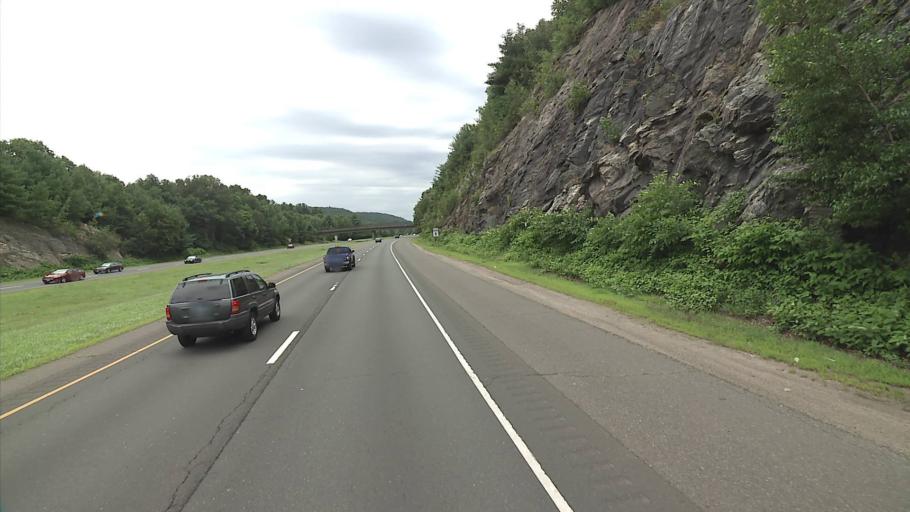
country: US
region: Connecticut
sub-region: New Haven County
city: Seymour
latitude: 41.4418
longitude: -73.0670
